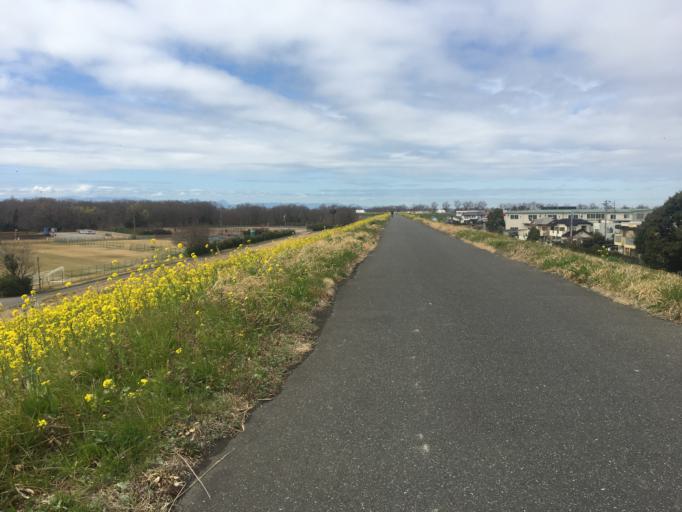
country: JP
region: Saitama
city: Shiki
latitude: 35.8572
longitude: 139.6018
